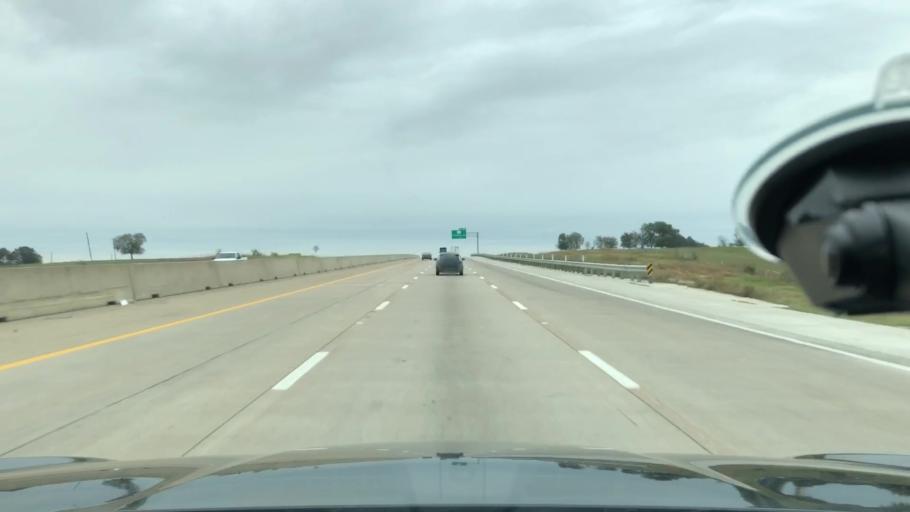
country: US
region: Texas
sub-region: Ellis County
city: Italy
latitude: 32.2388
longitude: -96.8783
